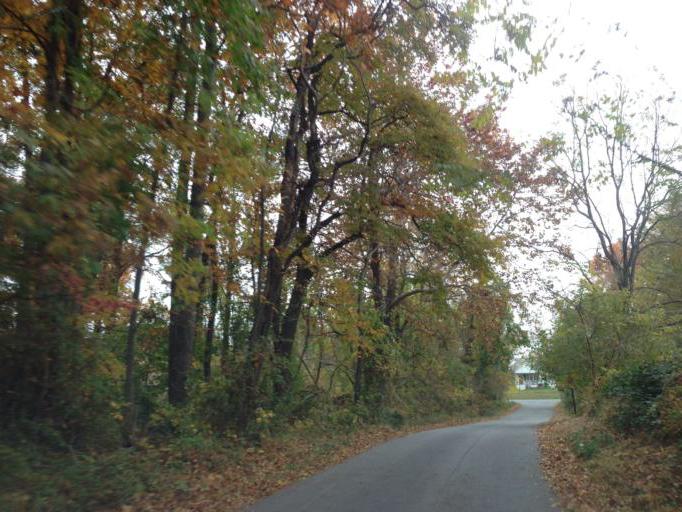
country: US
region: Maryland
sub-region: Baltimore County
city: Randallstown
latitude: 39.3942
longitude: -76.8610
